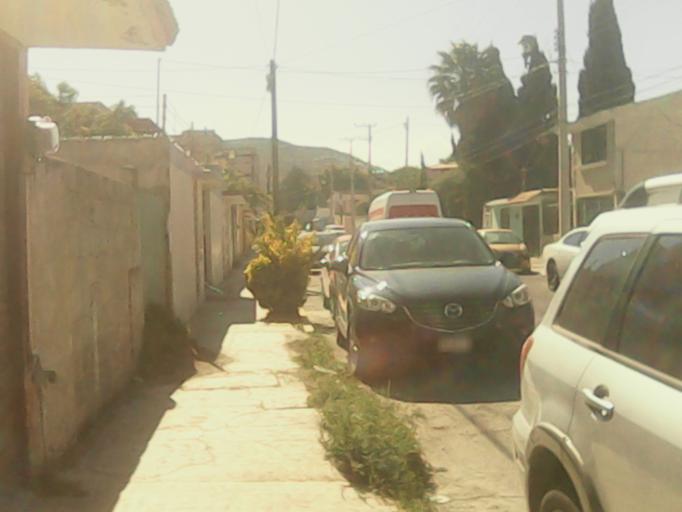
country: MX
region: Hidalgo
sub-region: Mineral de la Reforma
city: Campestre Villas del Alamo
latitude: 20.0971
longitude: -98.7132
